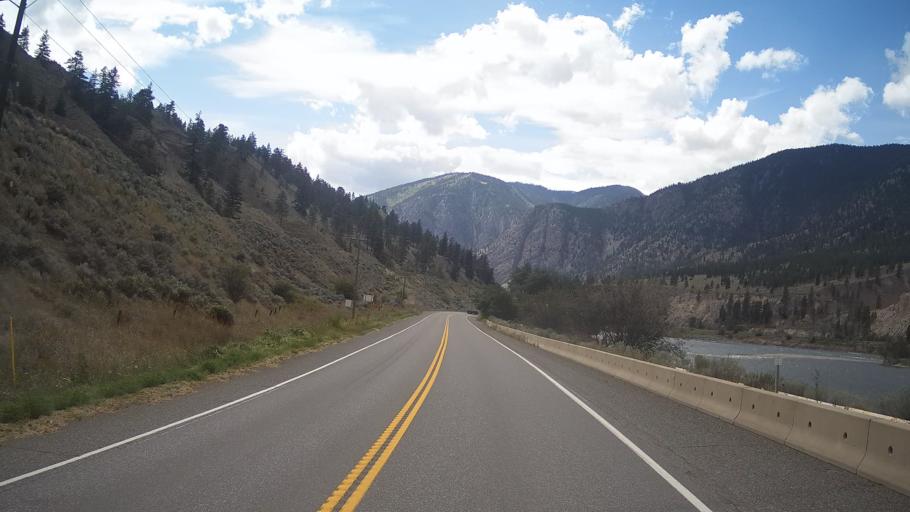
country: CA
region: British Columbia
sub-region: Thompson-Nicola Regional District
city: Ashcroft
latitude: 50.4056
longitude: -121.3723
